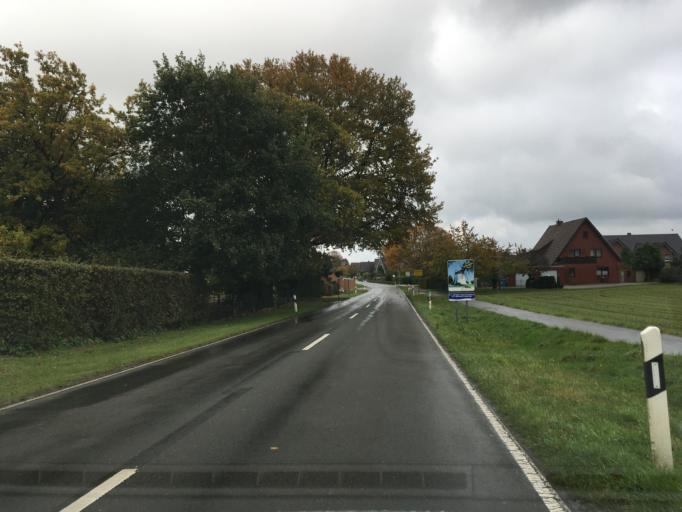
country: DE
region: North Rhine-Westphalia
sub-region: Regierungsbezirk Munster
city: Klein Reken
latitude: 51.8328
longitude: 7.0333
